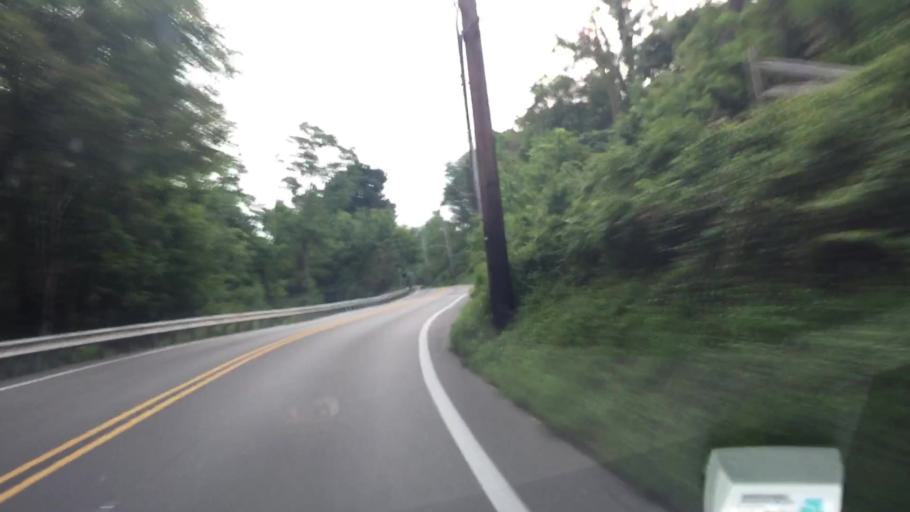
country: US
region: Pennsylvania
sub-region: Allegheny County
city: Whitehall
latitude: 40.3729
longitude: -79.9960
